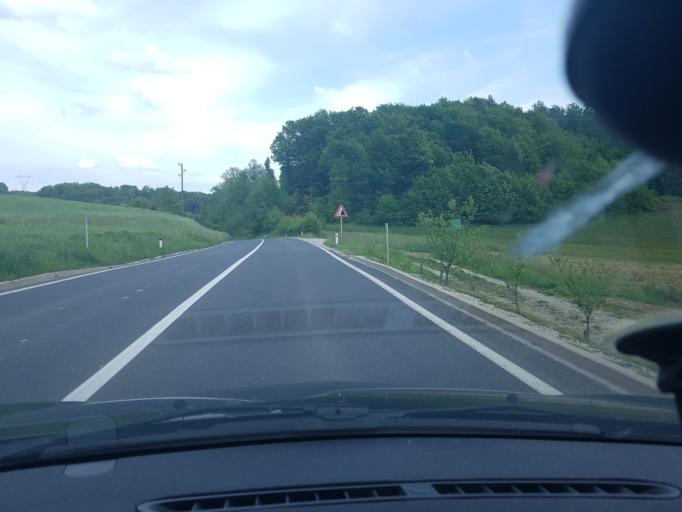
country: SI
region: Rogaska Slatina
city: Rogaska Slatina
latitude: 46.2517
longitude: 15.6314
